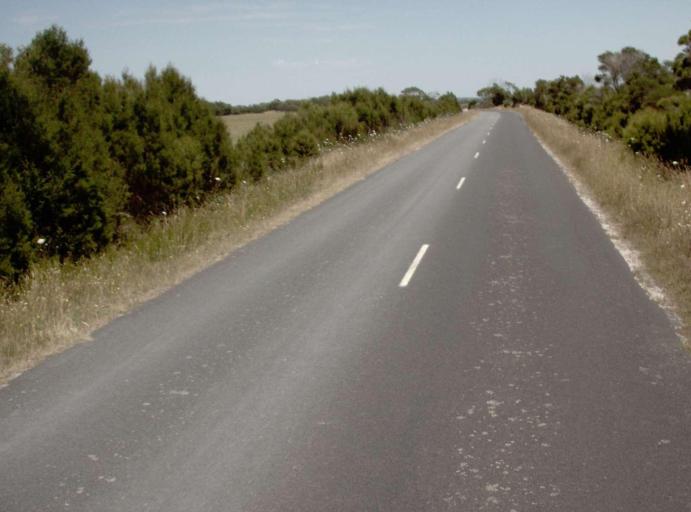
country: AU
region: Victoria
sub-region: Bass Coast
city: North Wonthaggi
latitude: -38.6649
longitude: 145.9937
